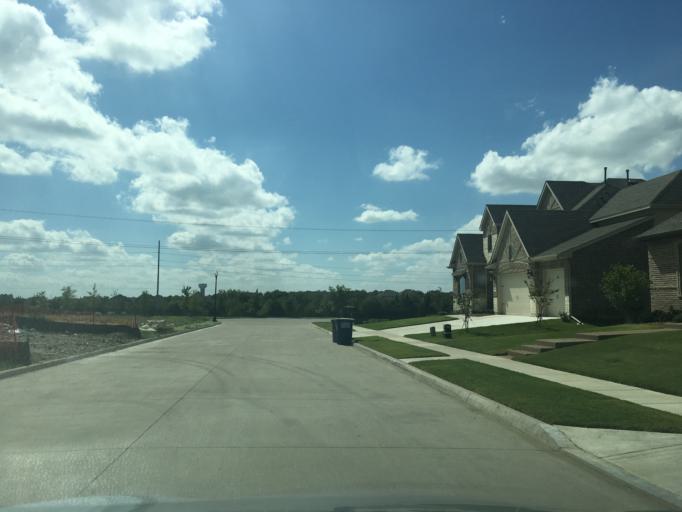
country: US
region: Texas
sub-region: Dallas County
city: Sachse
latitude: 32.9688
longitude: -96.5738
